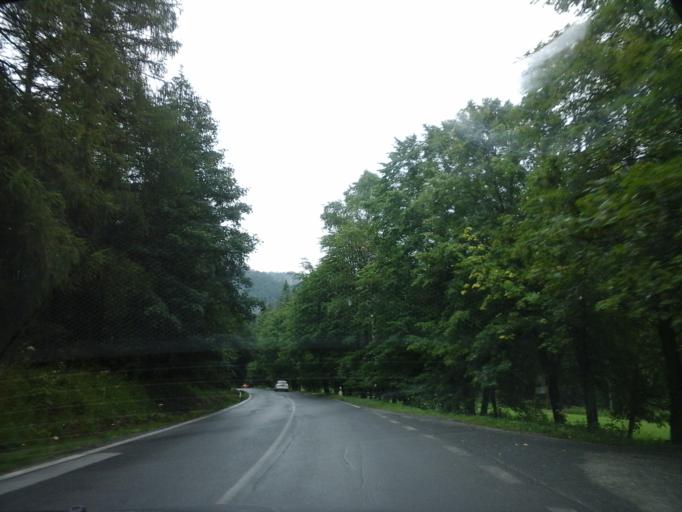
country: SK
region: Presovsky
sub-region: Okres Poprad
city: Zdiar
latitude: 49.2463
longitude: 20.3103
